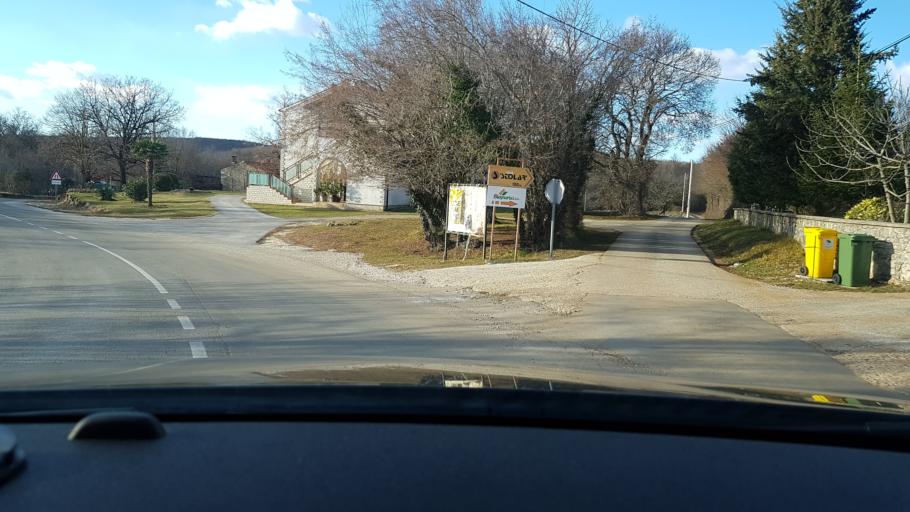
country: HR
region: Istarska
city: Vinez
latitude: 45.1050
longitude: 14.0970
